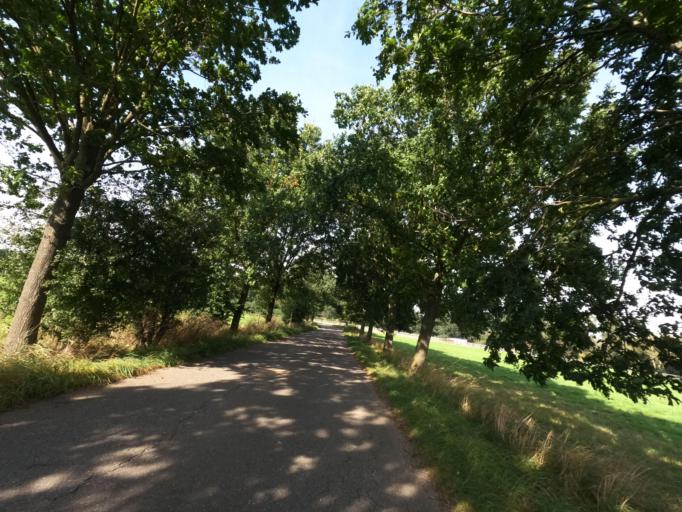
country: DE
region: North Rhine-Westphalia
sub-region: Regierungsbezirk Koln
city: Linnich
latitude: 50.9748
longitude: 6.2913
